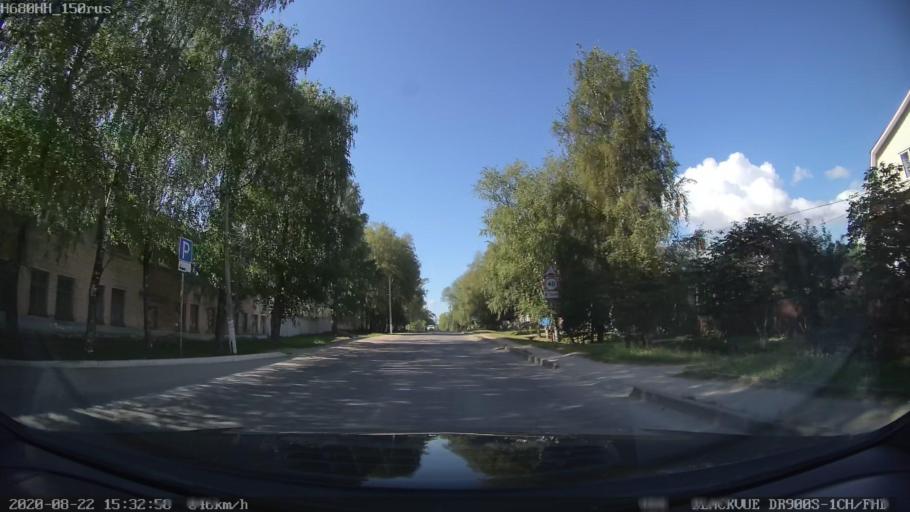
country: RU
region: Tverskaya
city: Bezhetsk
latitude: 57.7723
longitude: 36.7018
